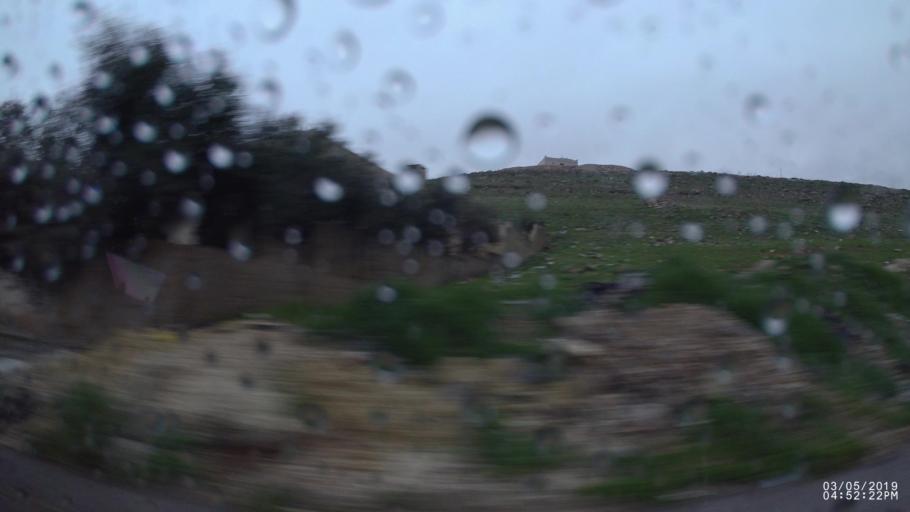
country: JO
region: Amman
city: Amman
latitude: 31.9938
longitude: 35.9709
